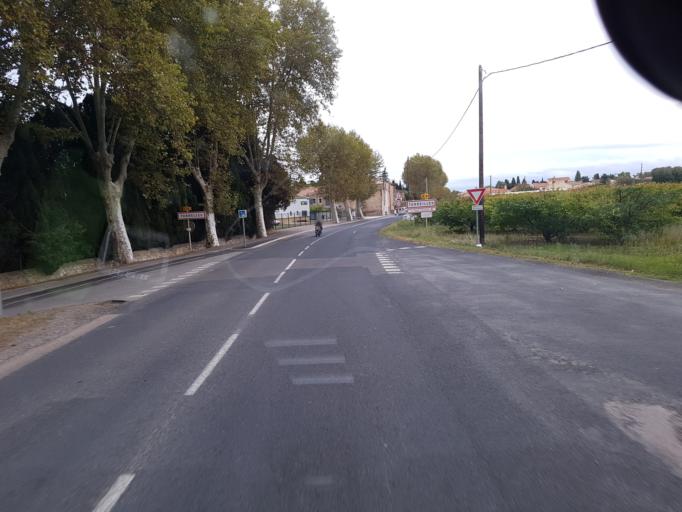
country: FR
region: Languedoc-Roussillon
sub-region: Departement des Pyrenees-Orientales
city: Torreilles
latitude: 42.7622
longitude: 2.9879
